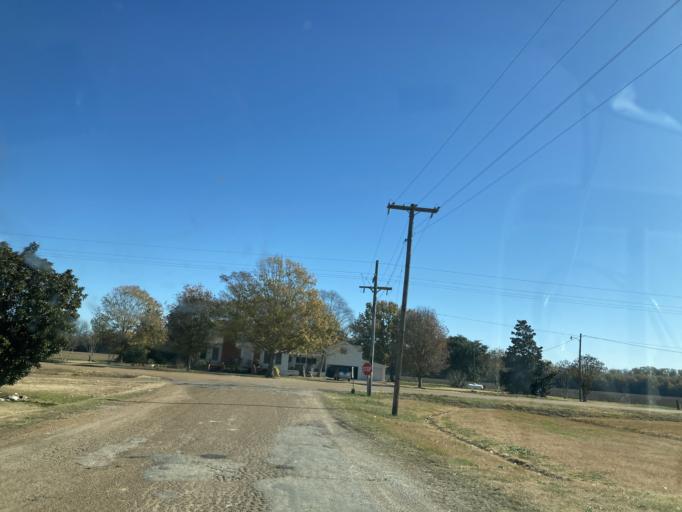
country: US
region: Mississippi
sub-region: Sharkey County
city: Rolling Fork
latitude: 32.8250
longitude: -90.7078
